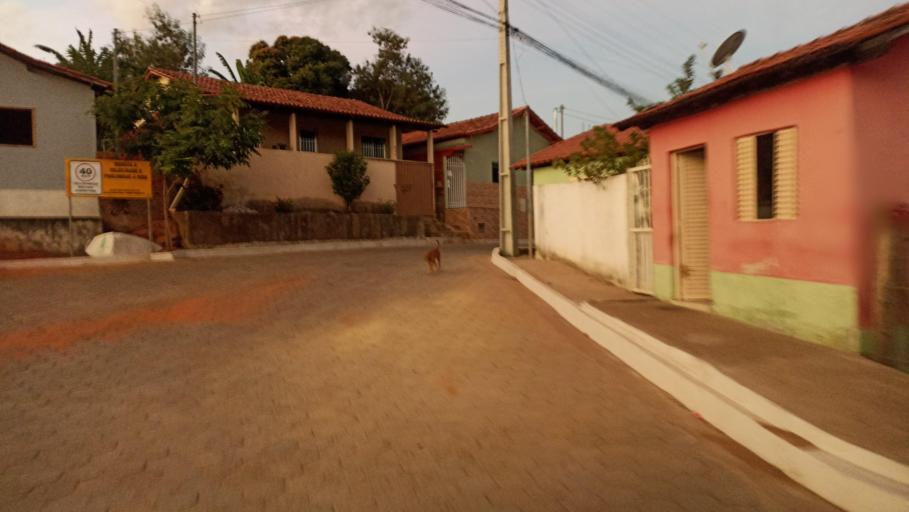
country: BR
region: Minas Gerais
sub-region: Aracuai
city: Aracuai
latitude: -16.6179
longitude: -42.1850
